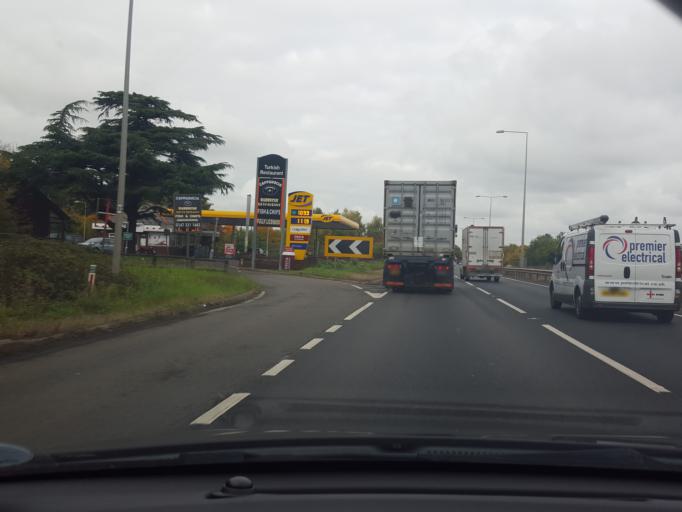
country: GB
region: England
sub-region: Suffolk
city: Capel Saint Mary
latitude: 52.0027
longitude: 1.0576
